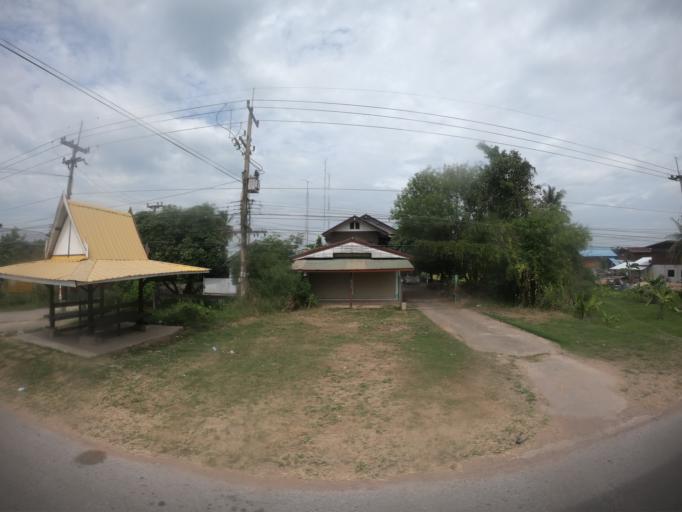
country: TH
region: Maha Sarakham
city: Maha Sarakham
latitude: 16.1516
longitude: 103.3806
